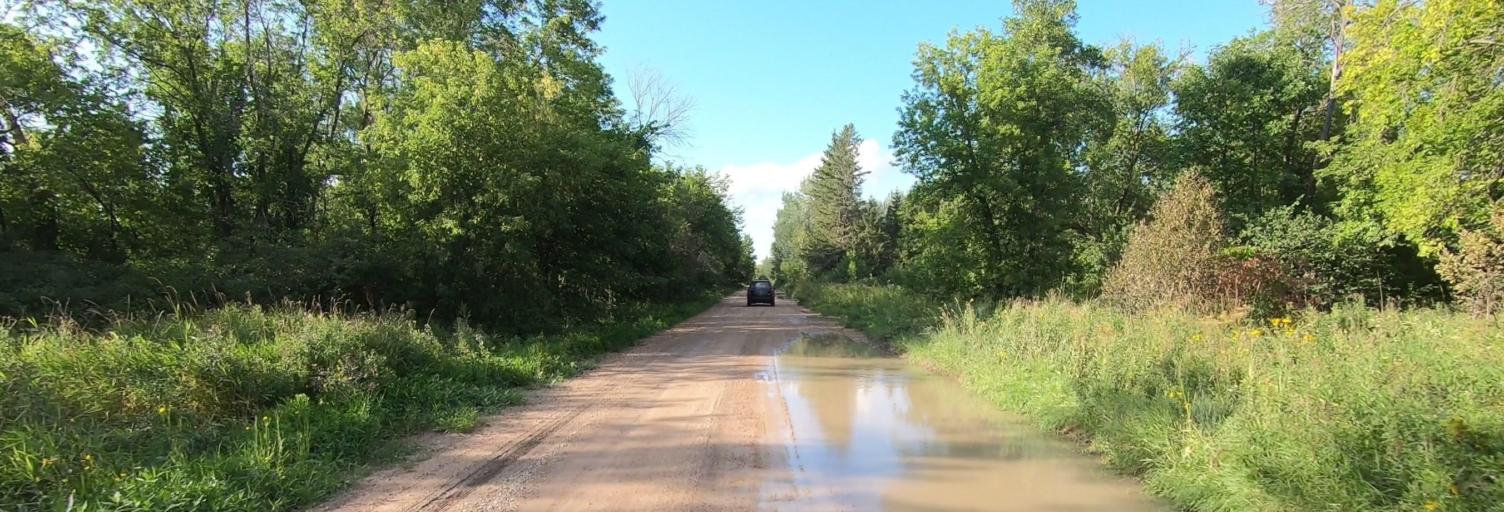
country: CA
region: Manitoba
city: Selkirk
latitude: 50.2706
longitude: -96.8496
